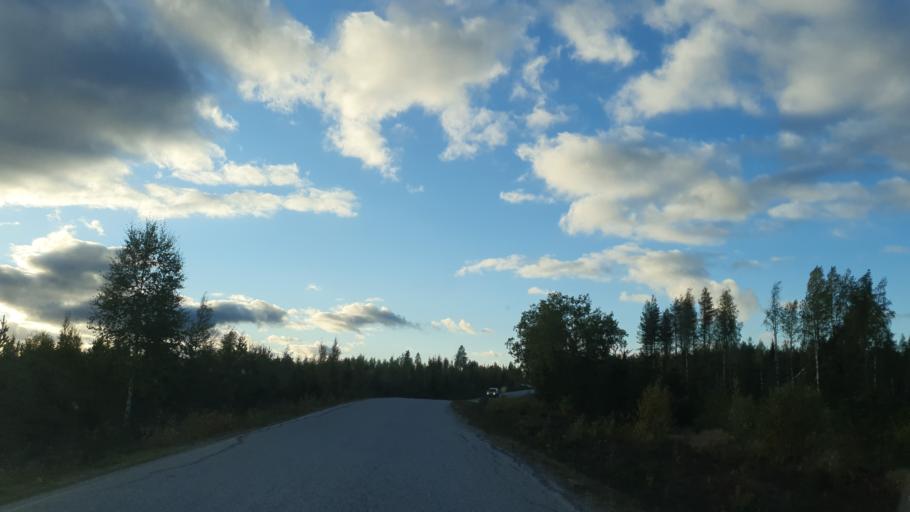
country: FI
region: Kainuu
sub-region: Kehys-Kainuu
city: Kuhmo
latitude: 63.9510
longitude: 29.7492
